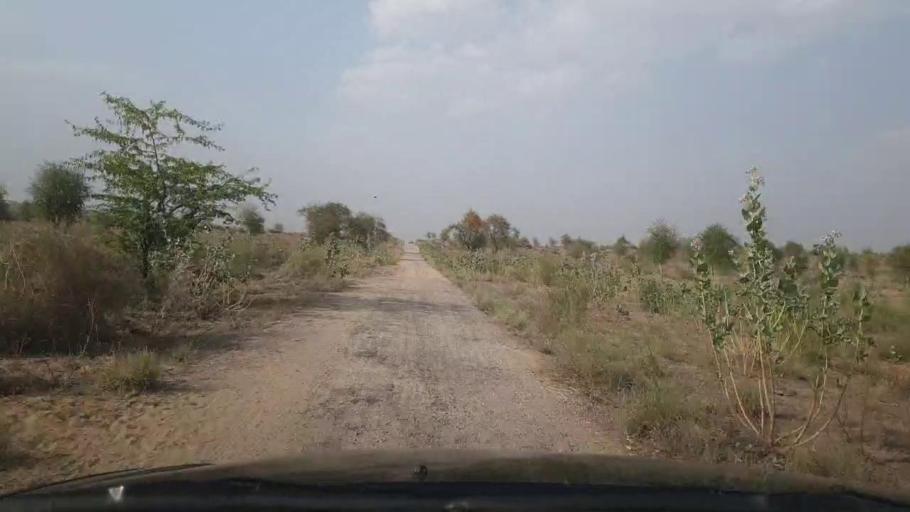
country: PK
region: Sindh
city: Islamkot
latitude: 25.0266
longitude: 70.5596
